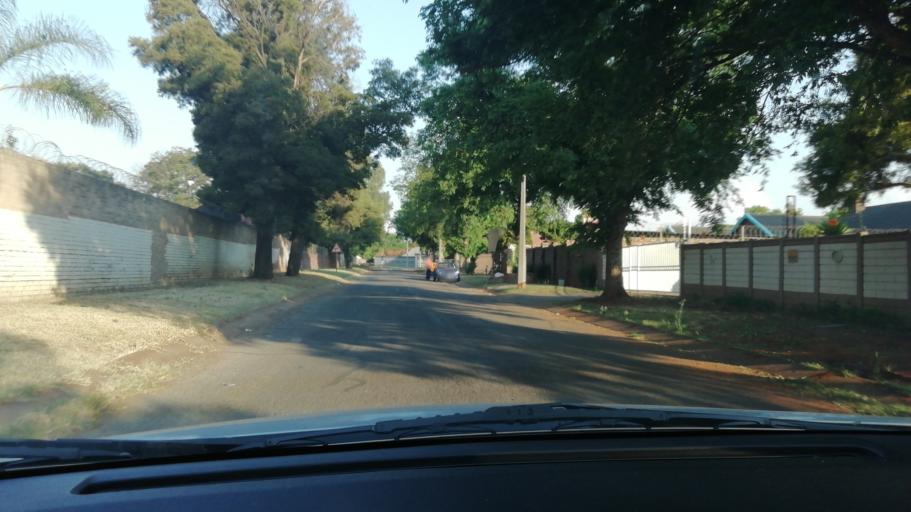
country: ZA
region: Gauteng
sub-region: Ekurhuleni Metropolitan Municipality
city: Benoni
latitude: -26.2002
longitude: 28.2946
